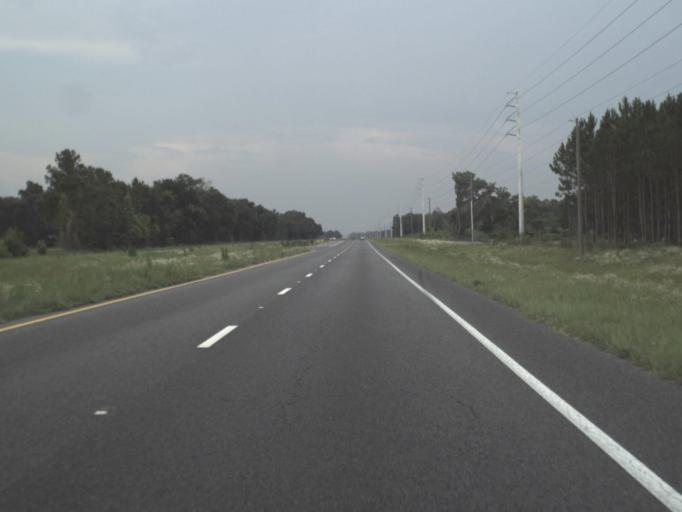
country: US
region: Florida
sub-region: Levy County
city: Chiefland
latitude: 29.4749
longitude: -82.7677
